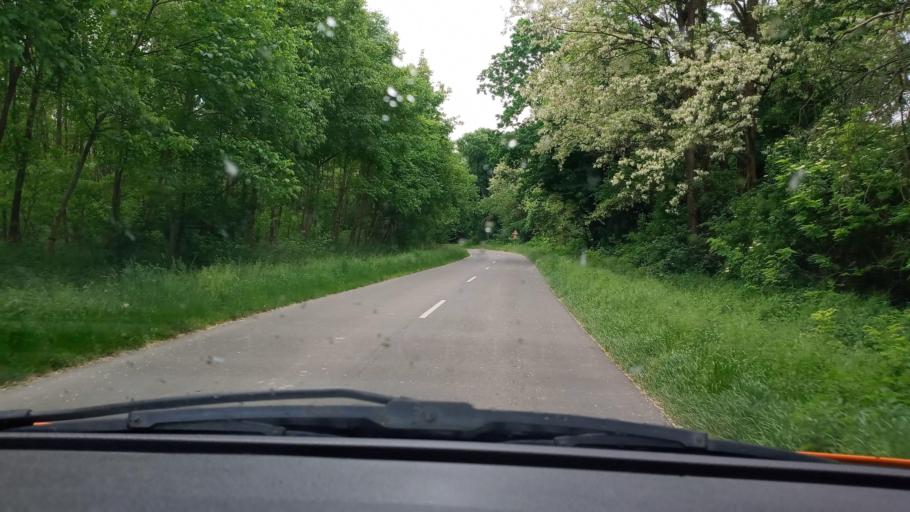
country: HU
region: Baranya
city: Vajszlo
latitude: 45.8315
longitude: 17.9726
